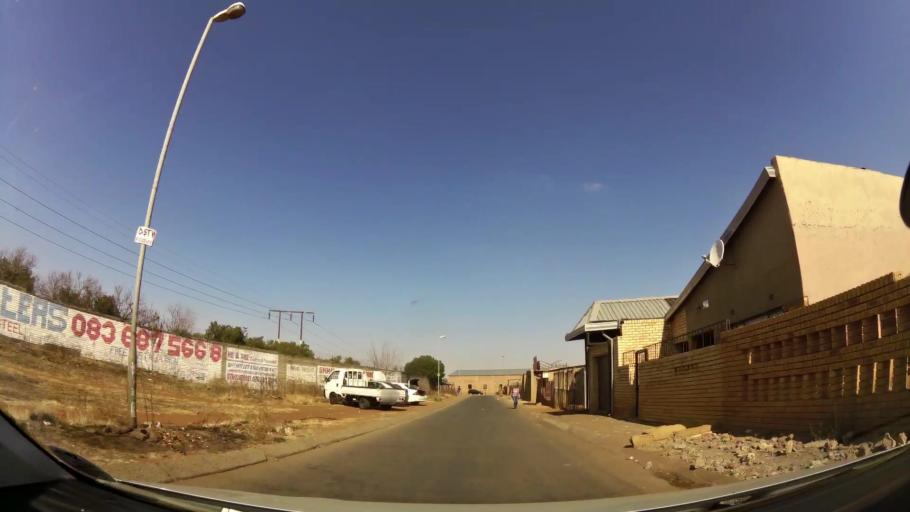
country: ZA
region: Gauteng
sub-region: City of Johannesburg Metropolitan Municipality
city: Soweto
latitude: -26.2805
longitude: 27.8627
